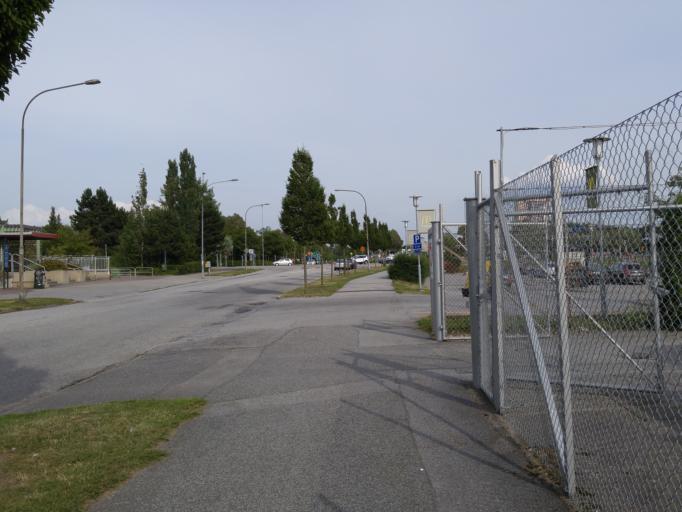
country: SE
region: Skane
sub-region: Lunds Kommun
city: Lund
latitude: 55.7210
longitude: 13.2003
